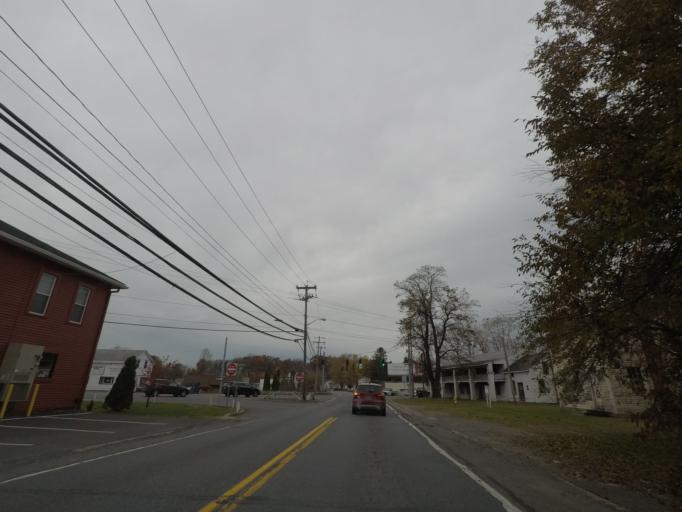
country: US
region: New York
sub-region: Saratoga County
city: Country Knolls
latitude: 42.8654
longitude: -73.7698
